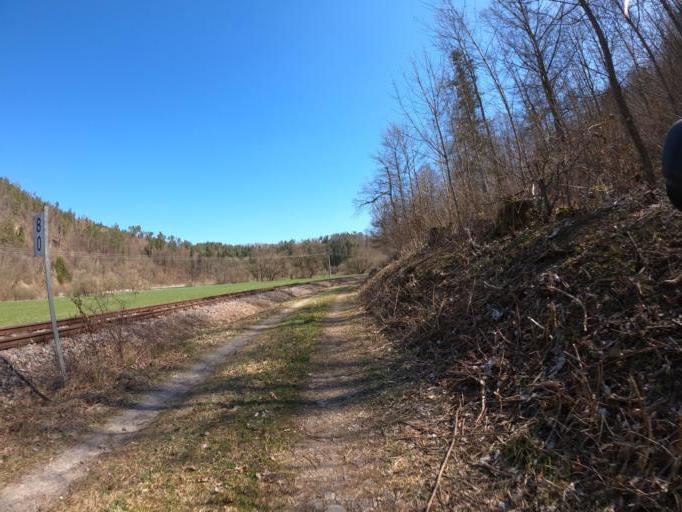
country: DE
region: Baden-Wuerttemberg
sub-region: Tuebingen Region
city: Haigerloch
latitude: 48.3905
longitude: 8.7852
